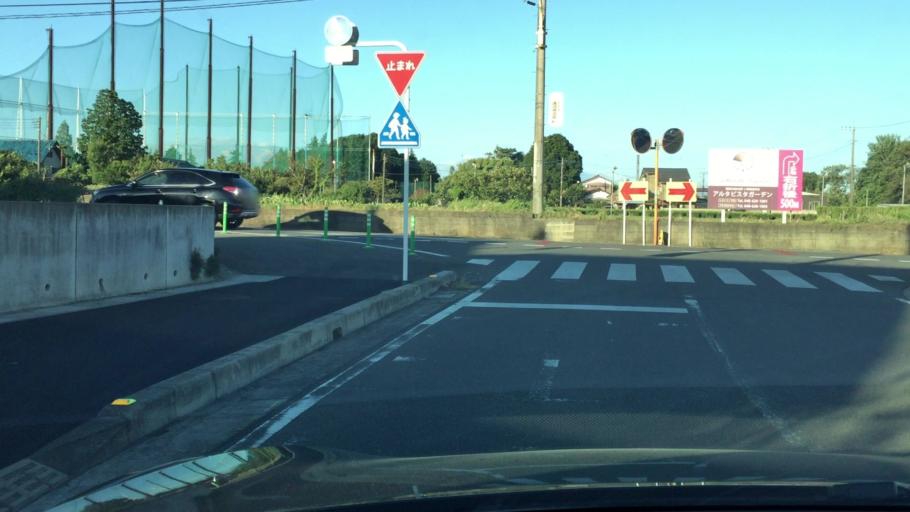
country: JP
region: Saitama
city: Ageoshimo
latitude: 35.9301
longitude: 139.5840
